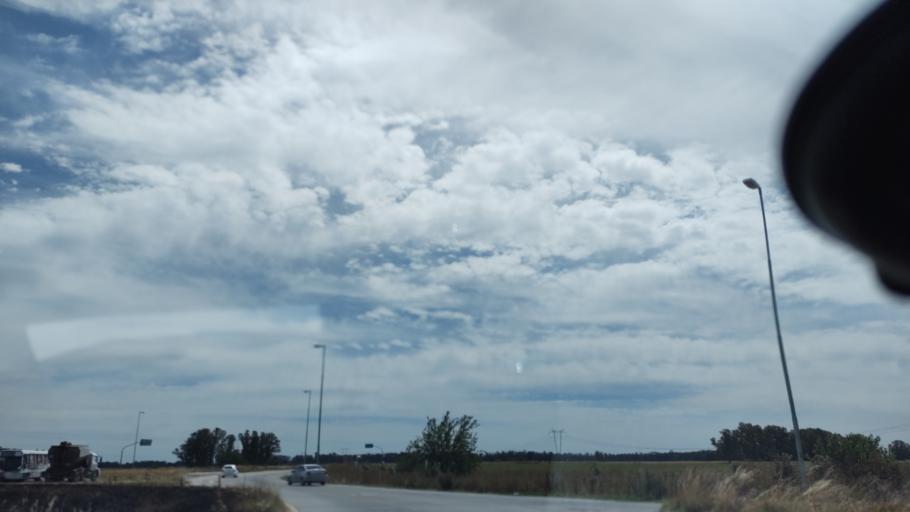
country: AR
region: Buenos Aires
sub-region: Partido de Brandsen
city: Brandsen
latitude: -35.0252
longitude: -58.2303
